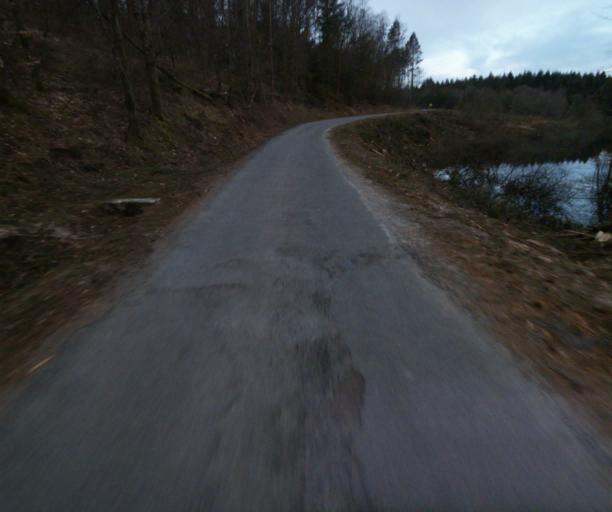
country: FR
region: Limousin
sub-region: Departement de la Correze
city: Correze
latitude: 45.4459
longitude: 1.8398
